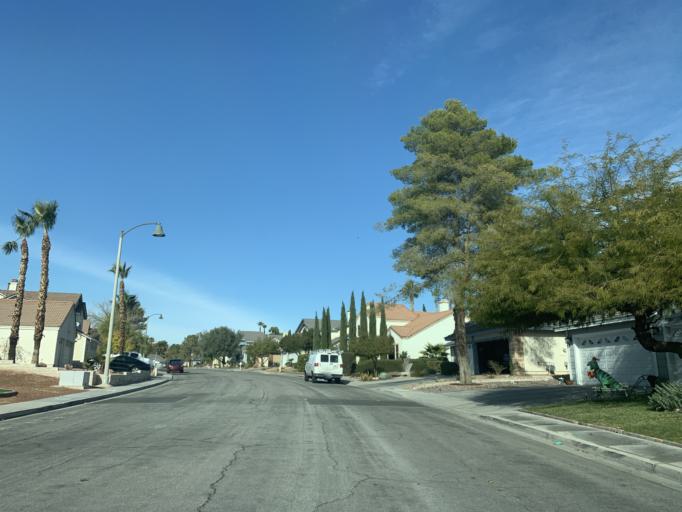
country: US
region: Nevada
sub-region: Clark County
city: Summerlin South
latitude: 36.1306
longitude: -115.2880
